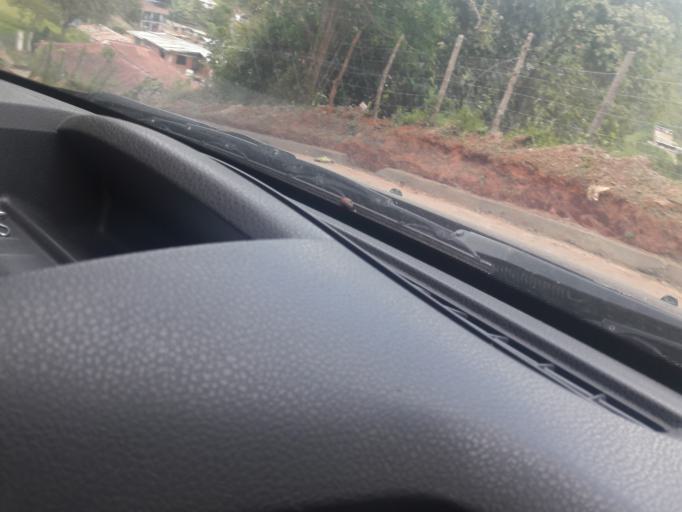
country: CO
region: Valle del Cauca
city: Cali
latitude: 3.4666
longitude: -76.6312
